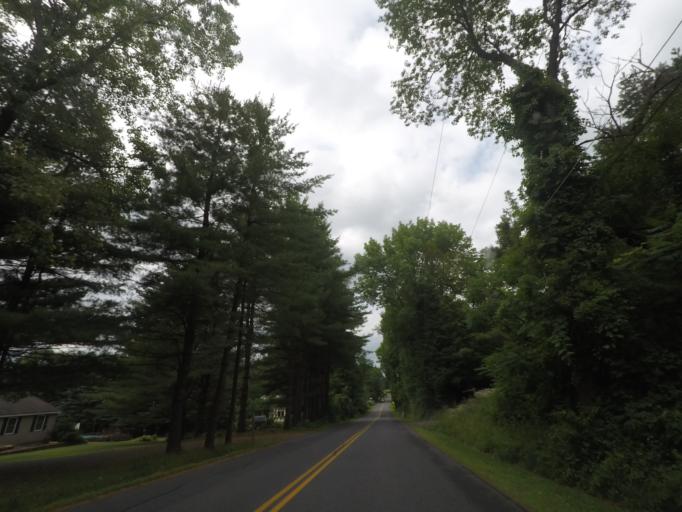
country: US
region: New York
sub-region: Saratoga County
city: Stillwater
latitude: 42.9975
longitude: -73.6932
